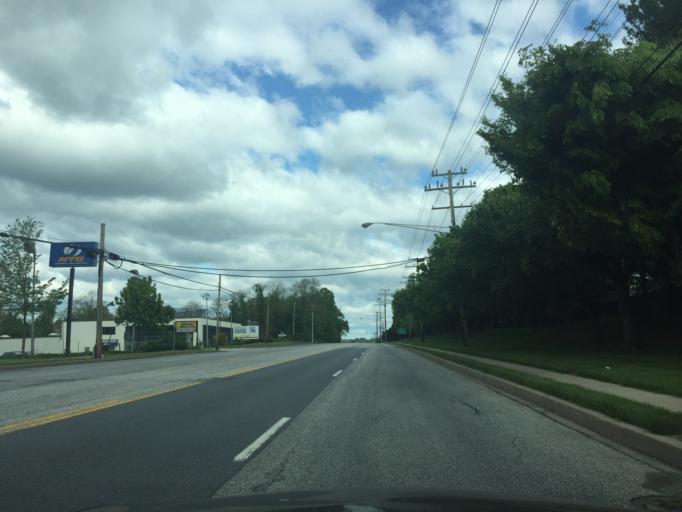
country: US
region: Maryland
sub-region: Baltimore County
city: Garrison
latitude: 39.4009
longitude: -76.7533
